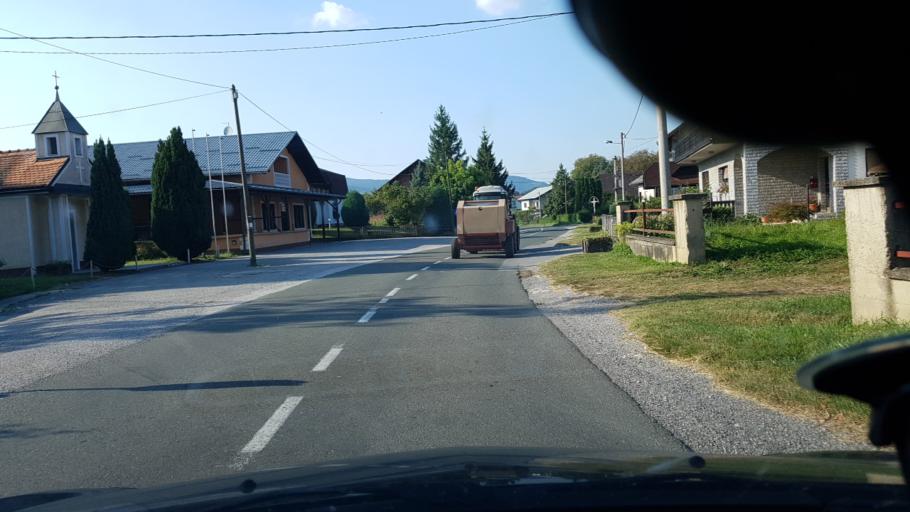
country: SI
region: Bistrica ob Sotli
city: Bistrica ob Sotli
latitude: 45.9911
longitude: 15.7238
